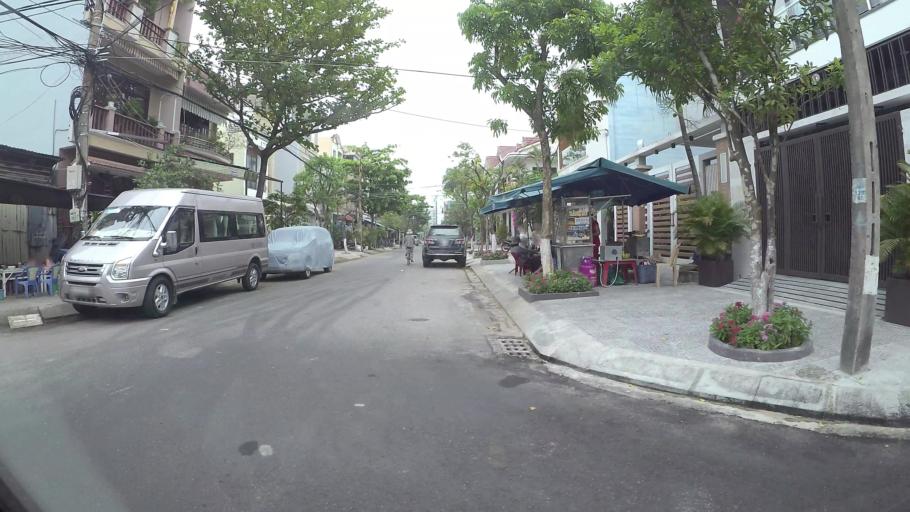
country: VN
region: Da Nang
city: Cam Le
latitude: 16.0310
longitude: 108.2264
